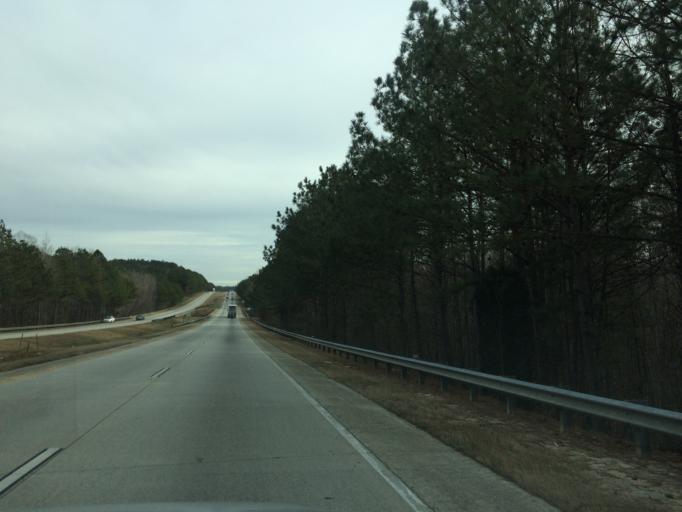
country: US
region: Georgia
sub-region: Barrow County
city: Auburn
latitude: 33.9704
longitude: -83.8367
